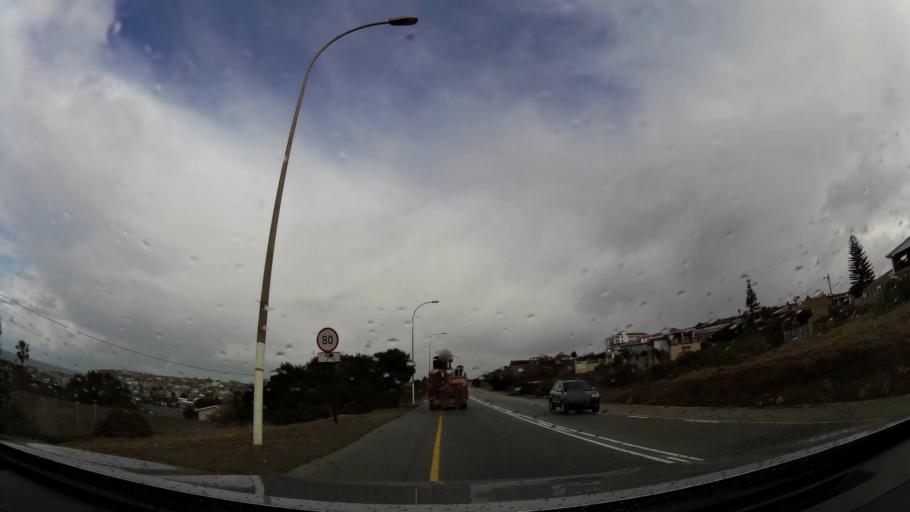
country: ZA
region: Western Cape
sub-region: Eden District Municipality
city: Mossel Bay
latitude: -34.1773
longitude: 22.1321
